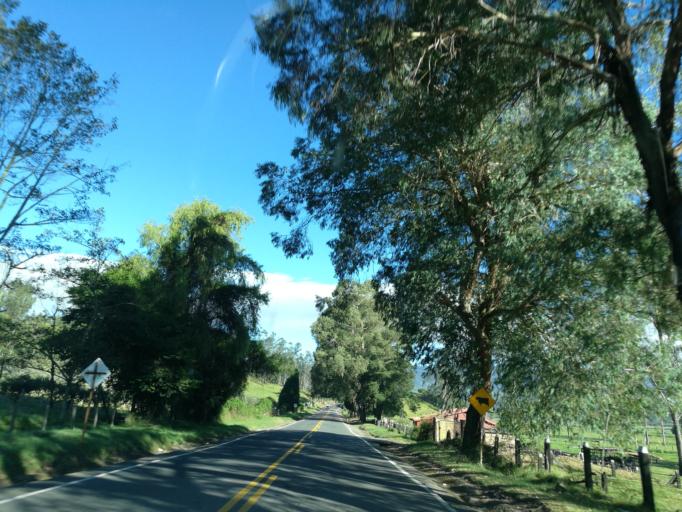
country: CO
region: Boyaca
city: Chiquinquira
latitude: 5.6245
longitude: -73.7868
